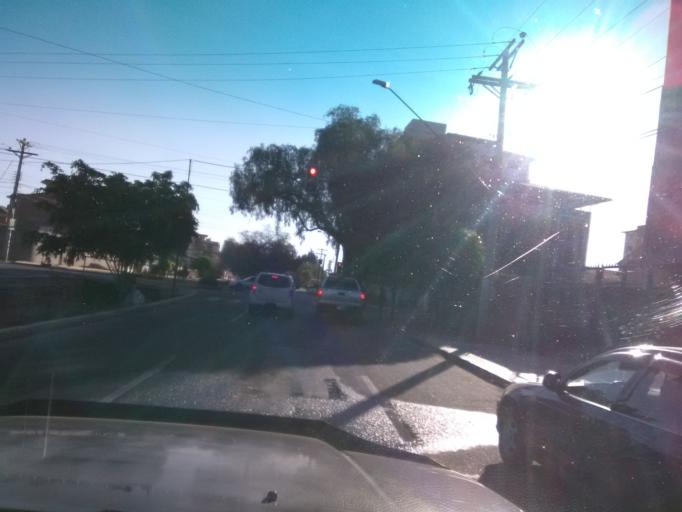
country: BO
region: Cochabamba
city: Cochabamba
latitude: -17.3812
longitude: -66.1986
